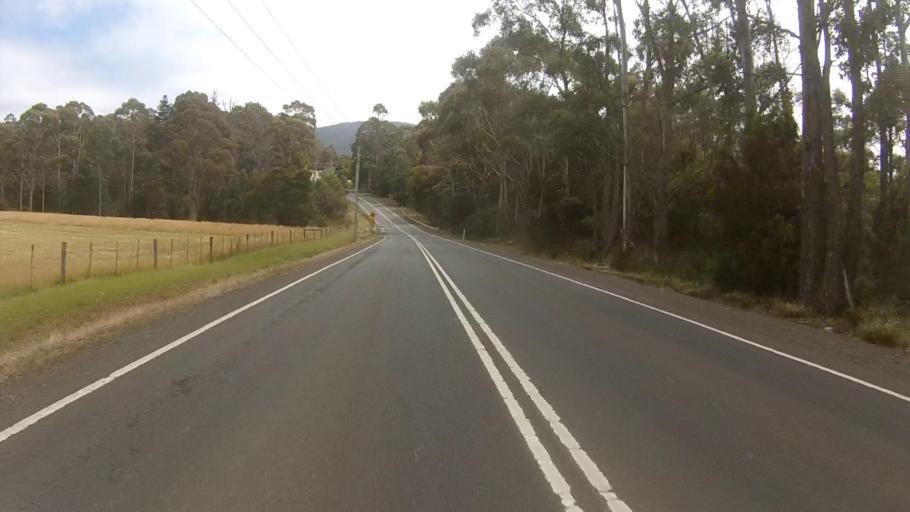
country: AU
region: Tasmania
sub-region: Kingborough
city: Margate
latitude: -42.9876
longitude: 147.1972
